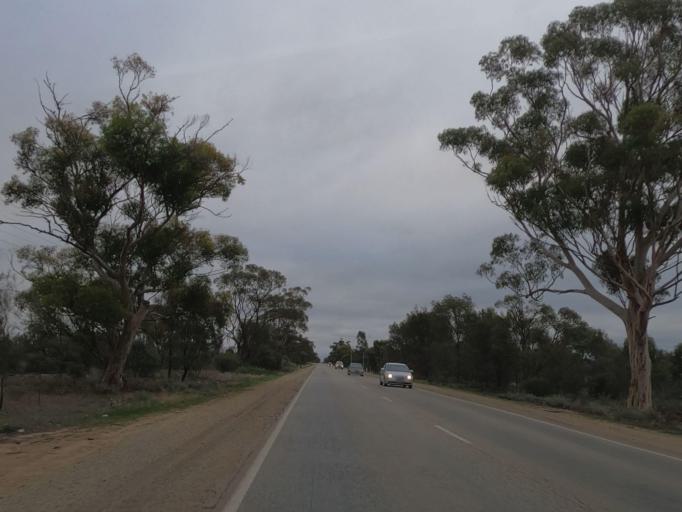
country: AU
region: Victoria
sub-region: Swan Hill
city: Swan Hill
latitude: -35.4100
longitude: 143.5847
